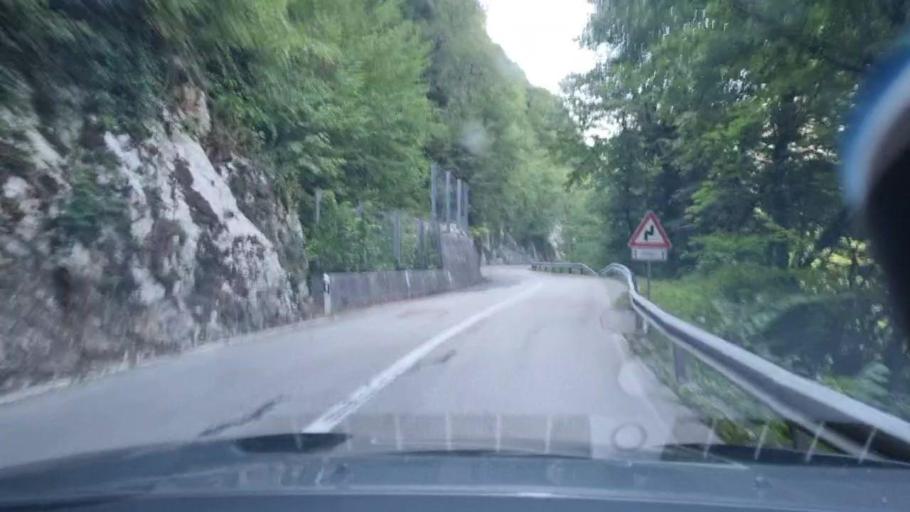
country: BA
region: Federation of Bosnia and Herzegovina
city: Stijena
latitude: 44.8846
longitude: 16.0597
